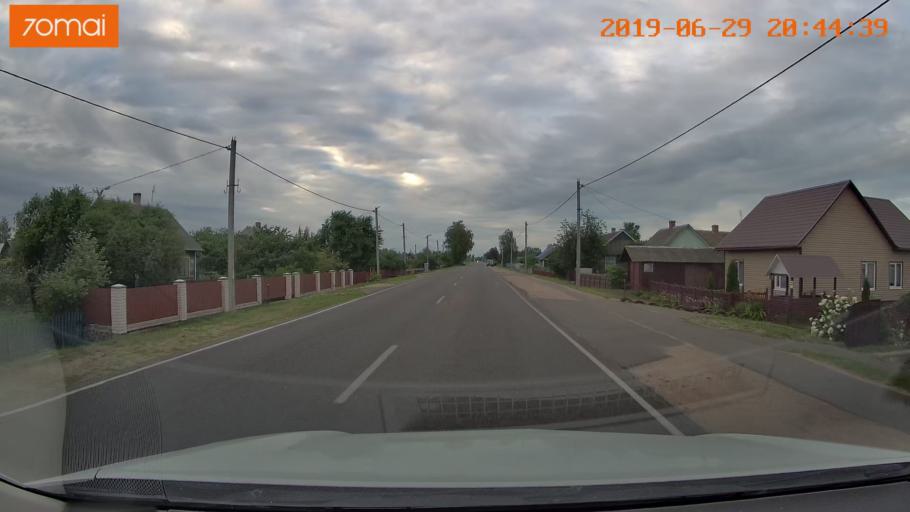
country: BY
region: Brest
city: Hantsavichy
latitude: 52.6157
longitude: 26.3074
